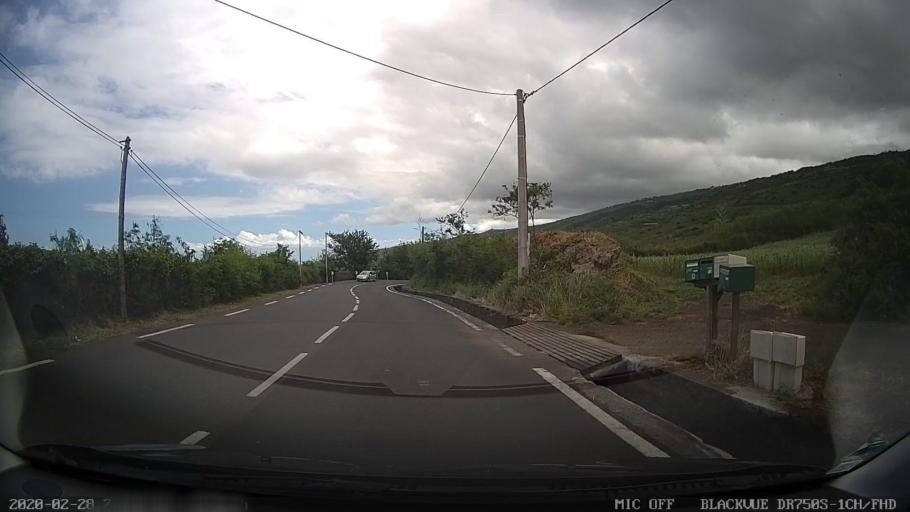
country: RE
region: Reunion
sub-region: Reunion
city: Saint-Leu
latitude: -21.1390
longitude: 55.2812
